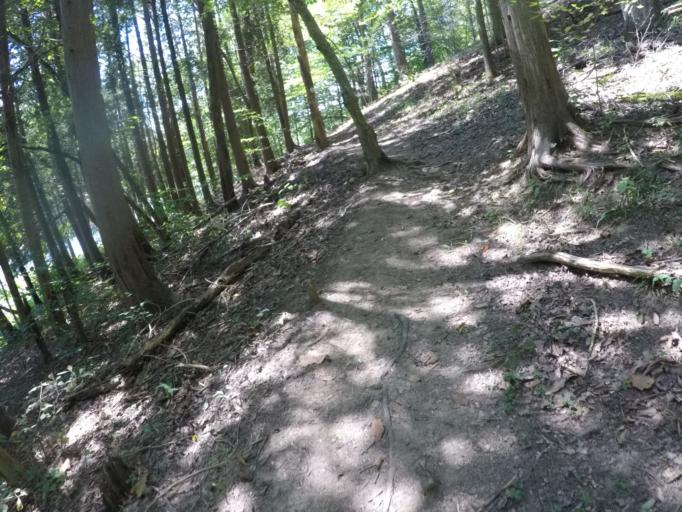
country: US
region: Ohio
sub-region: Lawrence County
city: Ironton
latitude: 38.6093
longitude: -82.6300
